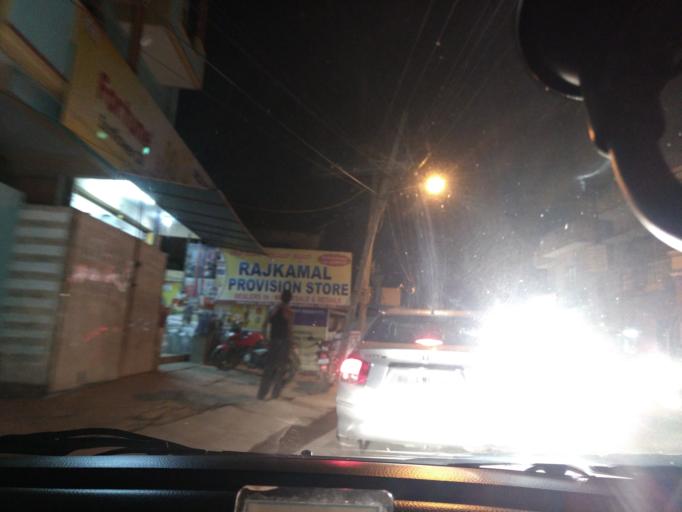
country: IN
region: Karnataka
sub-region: Bangalore Urban
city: Bangalore
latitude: 12.9021
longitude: 77.6605
